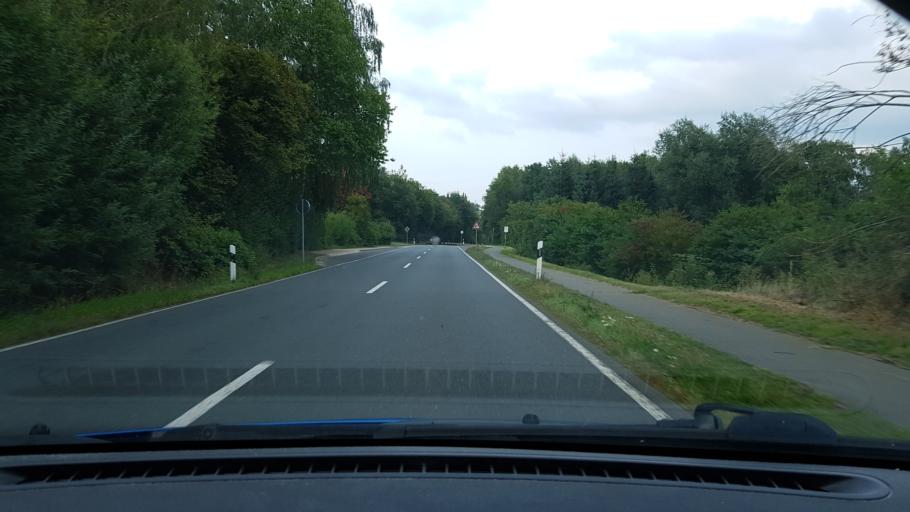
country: DE
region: Lower Saxony
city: Bad Munder am Deister
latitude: 52.1979
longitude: 9.4272
